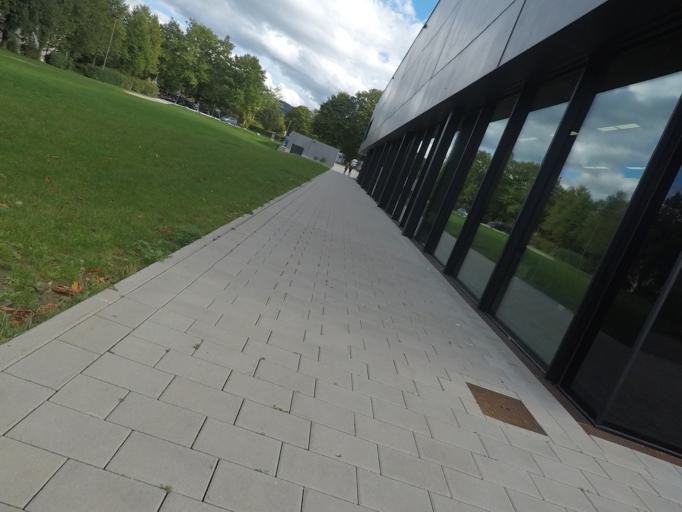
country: DE
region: Baden-Wuerttemberg
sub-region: Tuebingen Region
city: Pfullingen
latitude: 48.4562
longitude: 9.2267
